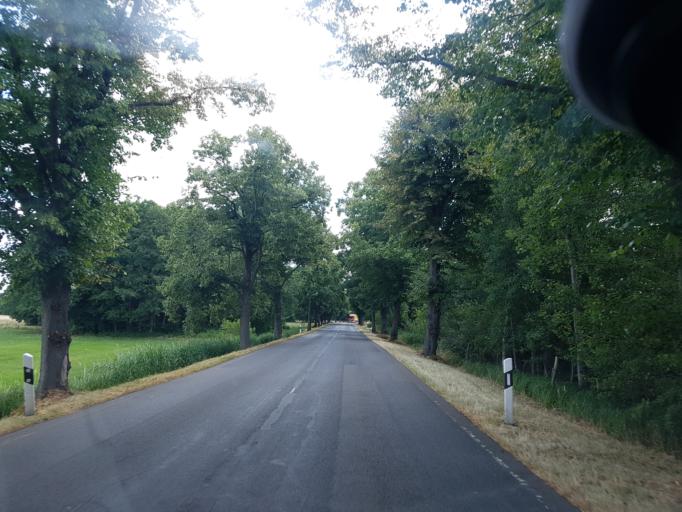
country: DE
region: Brandenburg
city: Drebkau
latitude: 51.6609
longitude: 14.2071
